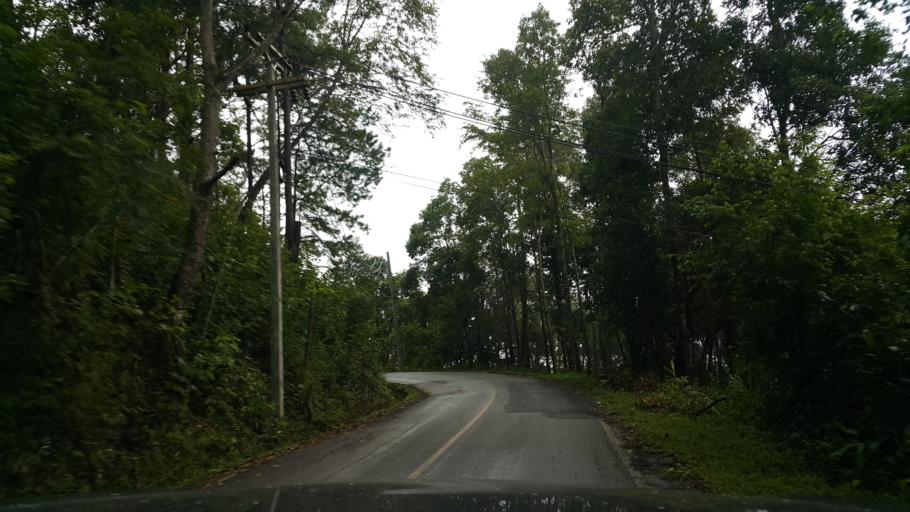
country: TH
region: Chiang Mai
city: Samoeng
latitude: 18.8829
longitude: 98.5255
